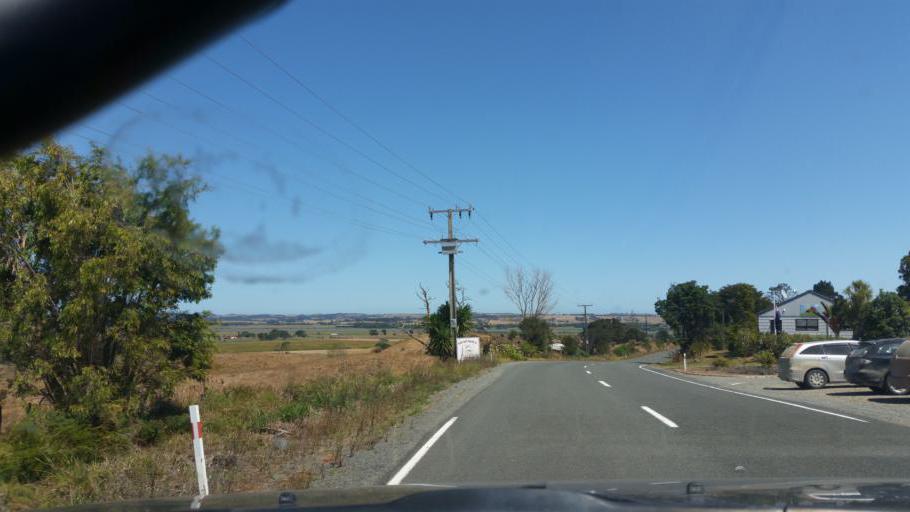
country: NZ
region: Northland
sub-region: Kaipara District
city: Dargaville
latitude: -36.0074
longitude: 173.9457
